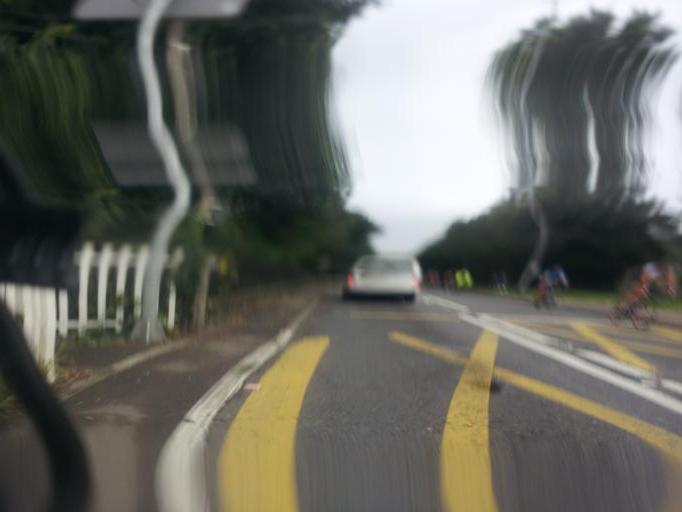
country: GB
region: England
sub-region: Kent
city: Aylesford
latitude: 51.3020
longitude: 0.4780
